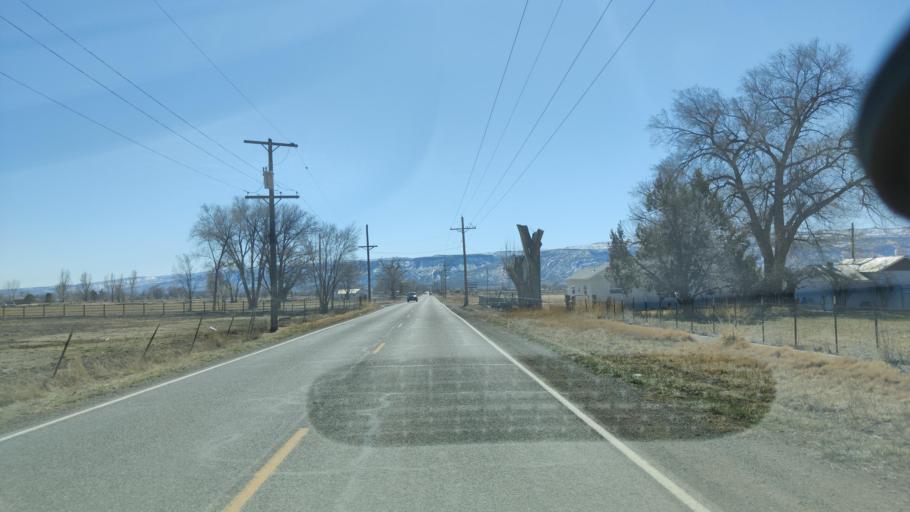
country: US
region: Colorado
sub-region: Mesa County
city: Fruita
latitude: 39.1615
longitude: -108.7011
